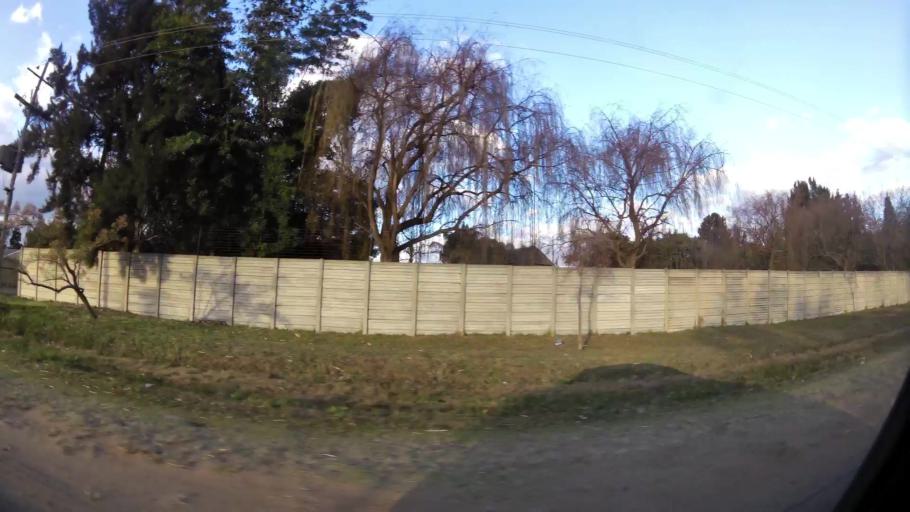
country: ZA
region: Gauteng
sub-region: City of Johannesburg Metropolitan Municipality
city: Midrand
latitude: -25.9785
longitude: 28.1531
